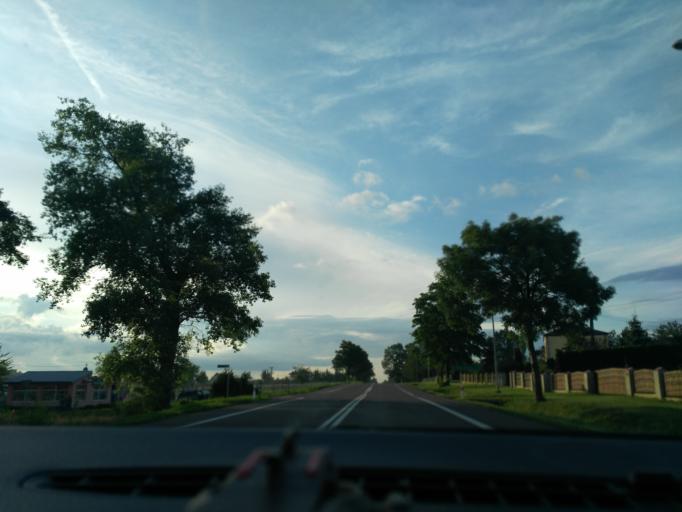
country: PL
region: Lublin Voivodeship
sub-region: Powiat lubelski
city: Niedrzwica Duza
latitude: 51.0612
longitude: 22.3827
